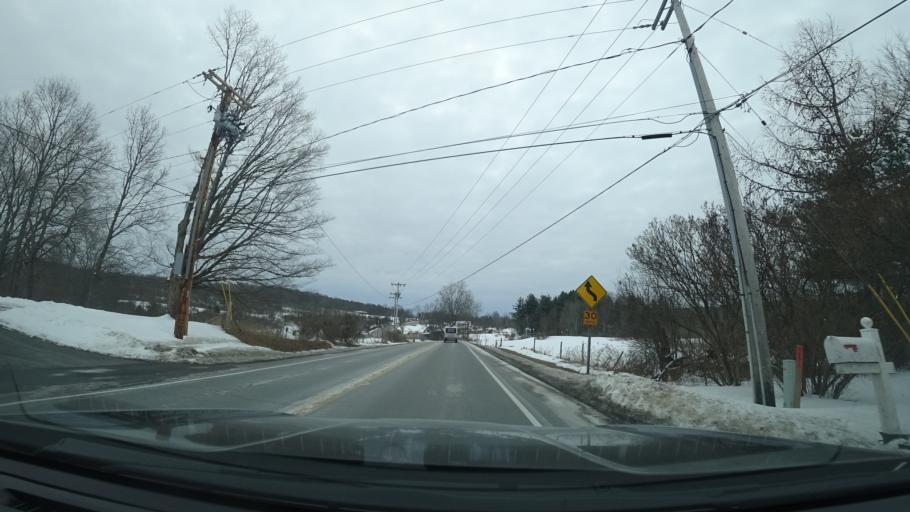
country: US
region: New York
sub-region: Washington County
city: Fort Edward
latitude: 43.2559
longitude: -73.5048
